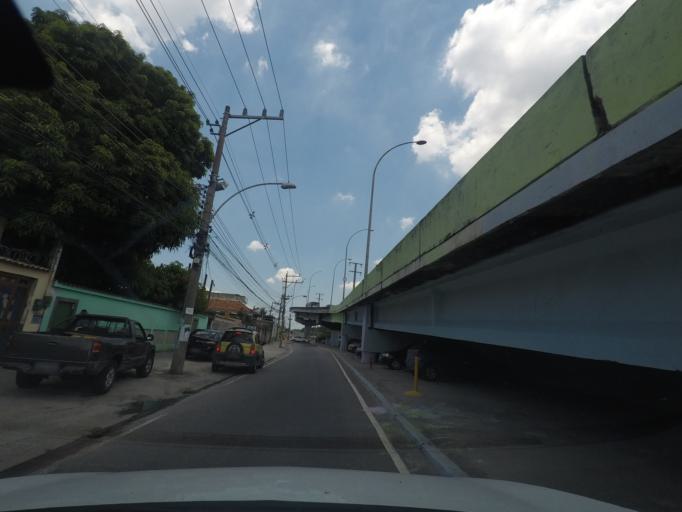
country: BR
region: Rio de Janeiro
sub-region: Sao Joao De Meriti
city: Sao Joao de Meriti
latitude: -22.8633
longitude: -43.3649
